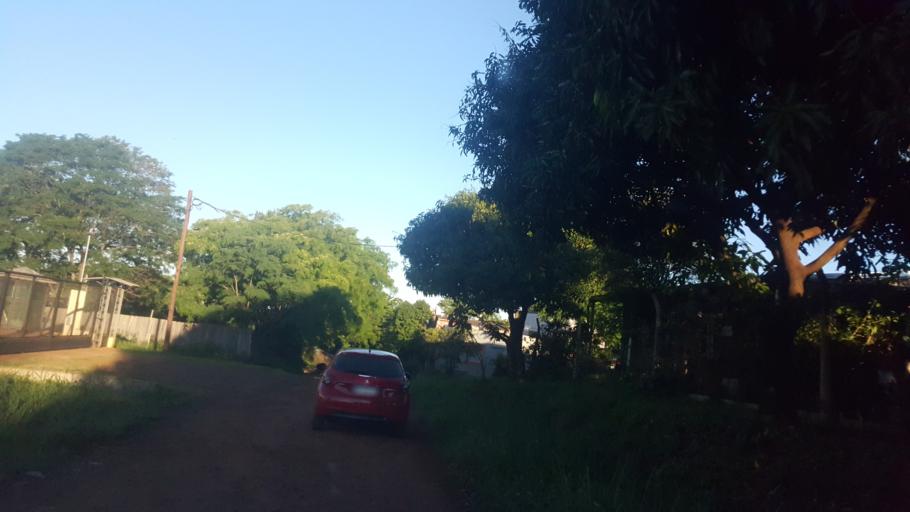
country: AR
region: Misiones
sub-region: Departamento de Capital
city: Posadas
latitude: -27.4239
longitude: -55.9151
